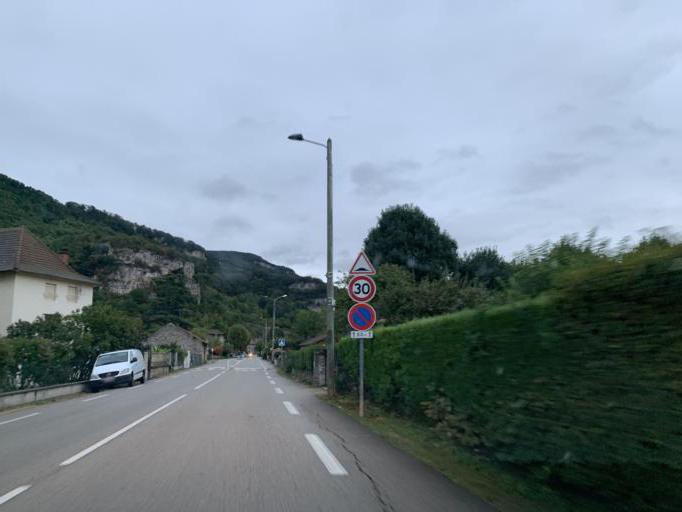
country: FR
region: Rhone-Alpes
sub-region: Departement de l'Ain
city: Saint-Sorlin-en-Bugey
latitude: 45.8854
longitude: 5.3666
